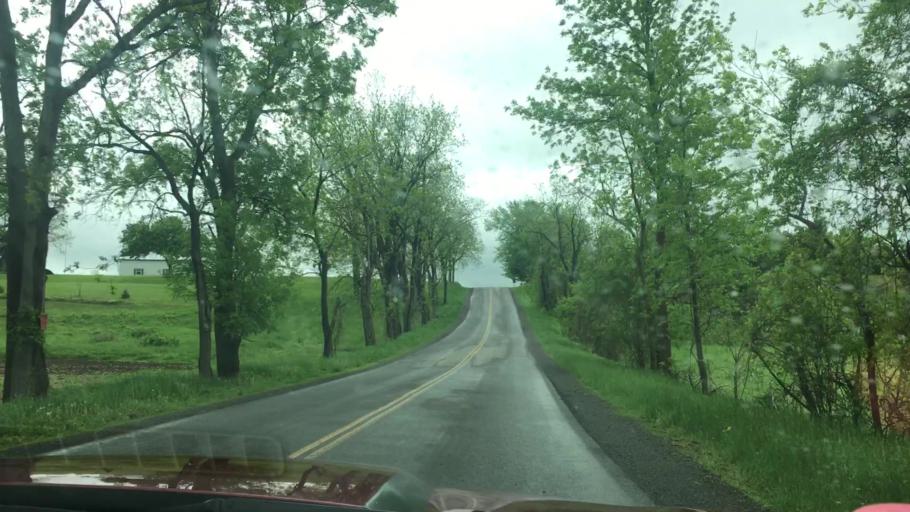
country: US
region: New York
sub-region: Genesee County
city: Batavia
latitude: 43.0859
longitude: -78.1394
